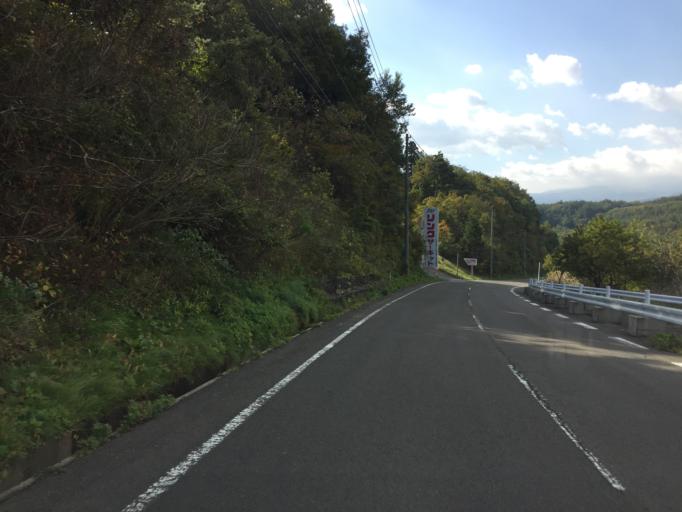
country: JP
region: Fukushima
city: Fukushima-shi
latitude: 37.8039
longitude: 140.3892
